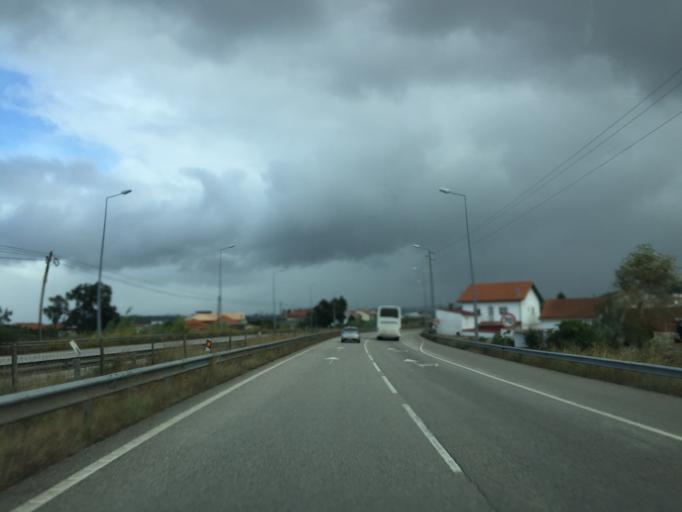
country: PT
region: Coimbra
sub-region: Coimbra
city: Coimbra
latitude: 40.2048
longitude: -8.4765
